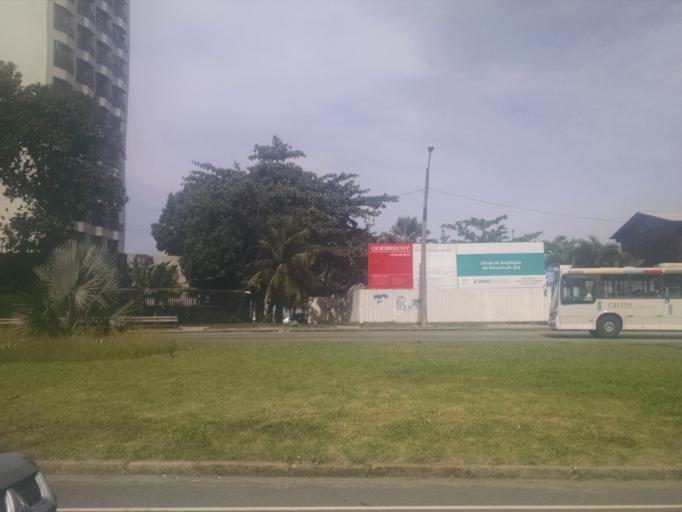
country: BR
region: Rio de Janeiro
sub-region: Rio De Janeiro
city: Rio de Janeiro
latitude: -22.9959
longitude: -43.2597
